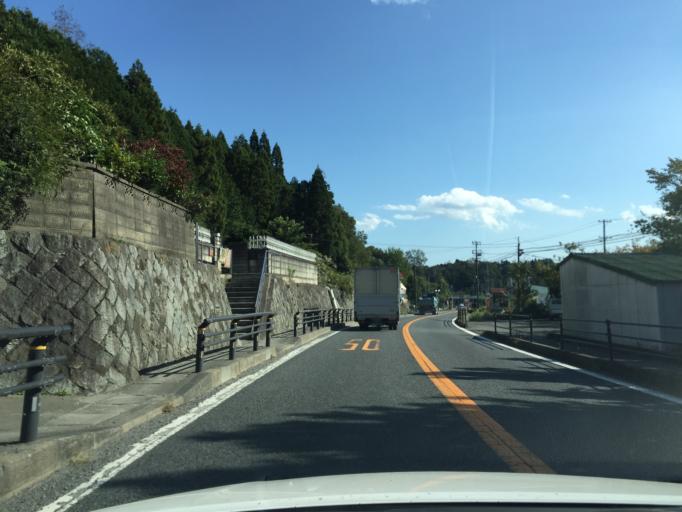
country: JP
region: Fukushima
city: Iwaki
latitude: 37.0738
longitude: 140.8271
